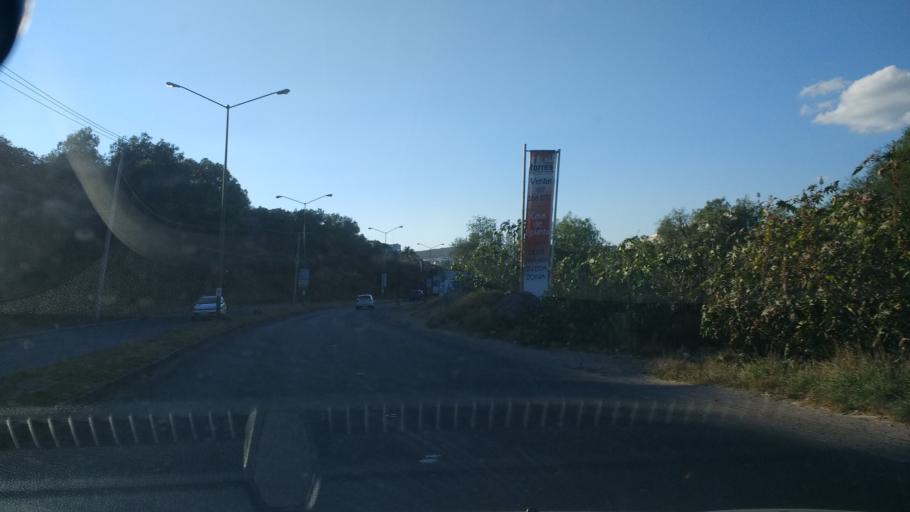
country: MX
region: Guanajuato
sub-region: Leon
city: La Ermita
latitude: 21.1765
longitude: -101.6999
